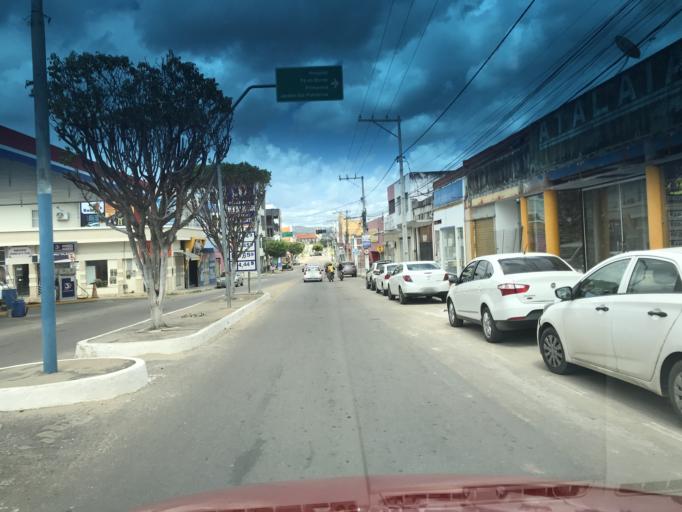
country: BR
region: Bahia
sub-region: Itaberaba
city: Itaberaba
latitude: -12.5300
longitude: -40.3080
